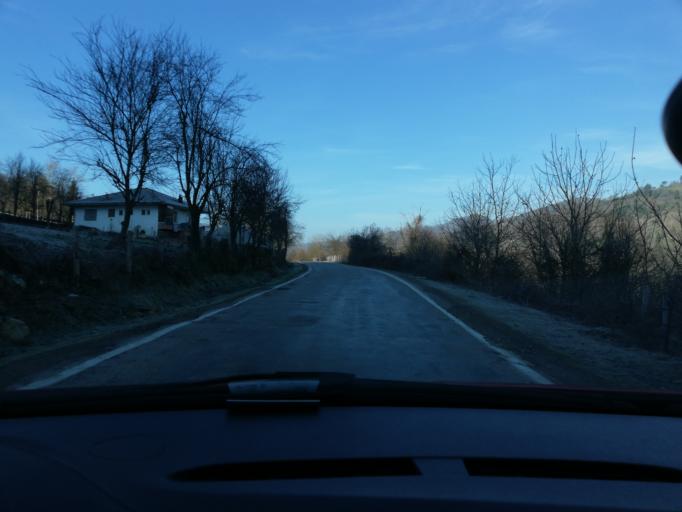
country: TR
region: Bartin
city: Kumluca
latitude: 41.4540
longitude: 32.5010
